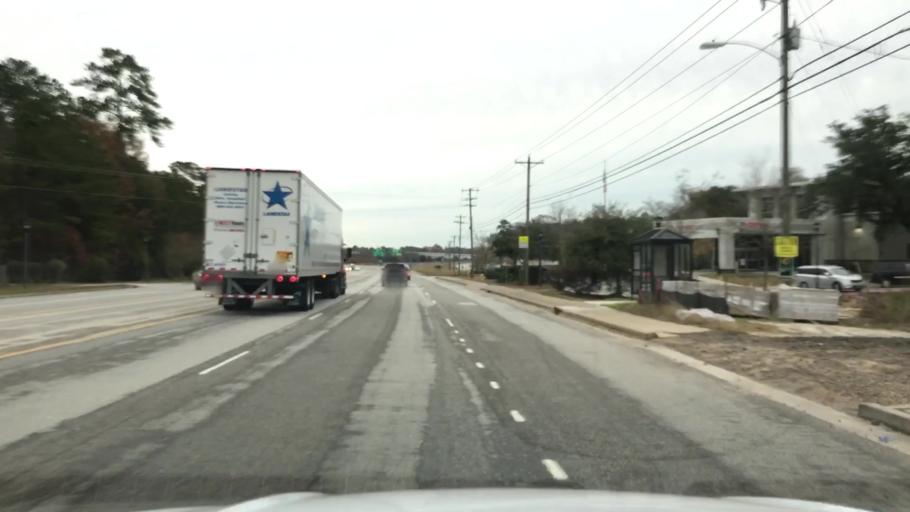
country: US
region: South Carolina
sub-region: Berkeley County
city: Goose Creek
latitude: 32.9737
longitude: -80.0566
